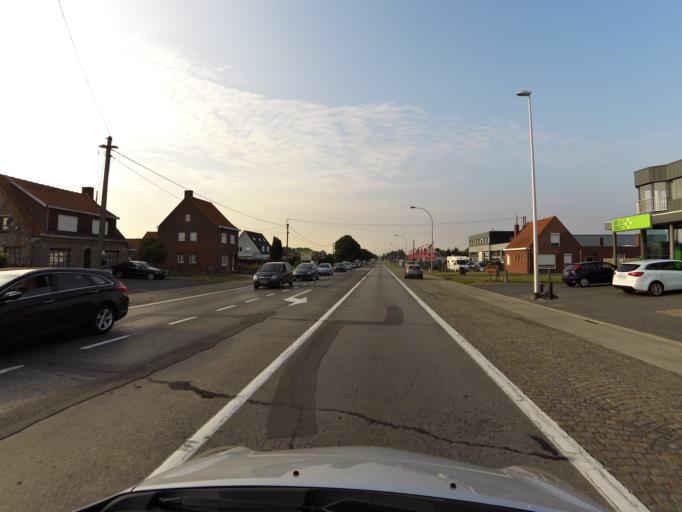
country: BE
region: Flanders
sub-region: Provincie West-Vlaanderen
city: Torhout
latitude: 51.0325
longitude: 3.1095
